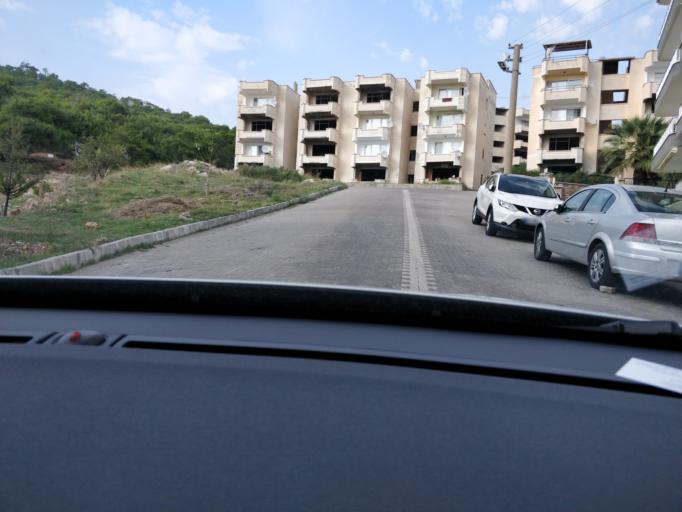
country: TR
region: Balikesir
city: Ayvalik
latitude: 39.2732
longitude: 26.6502
